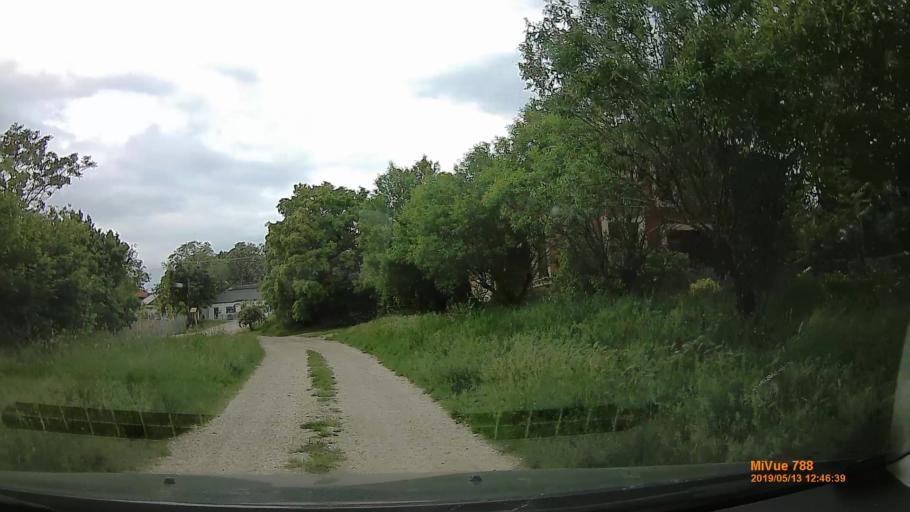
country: HU
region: Pest
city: Diosd
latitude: 47.4047
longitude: 18.9863
